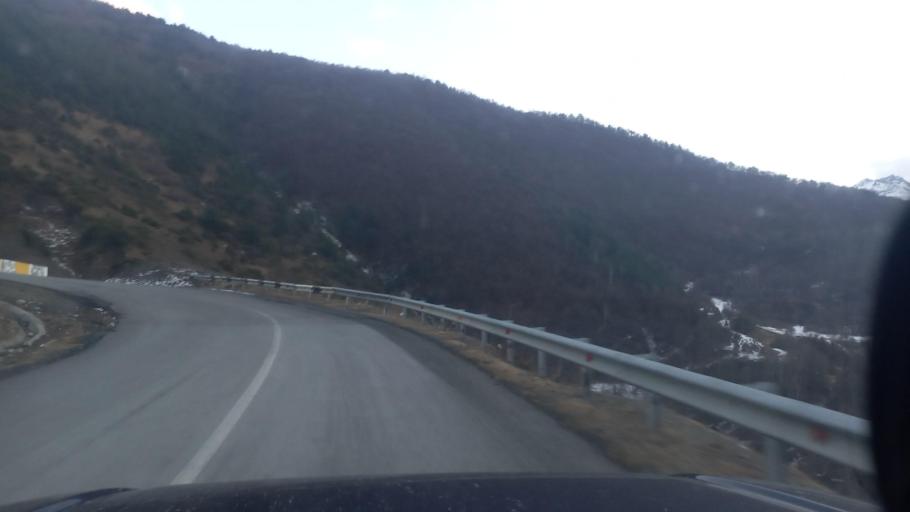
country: RU
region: Ingushetiya
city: Dzhayrakh
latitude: 42.8095
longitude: 44.7984
